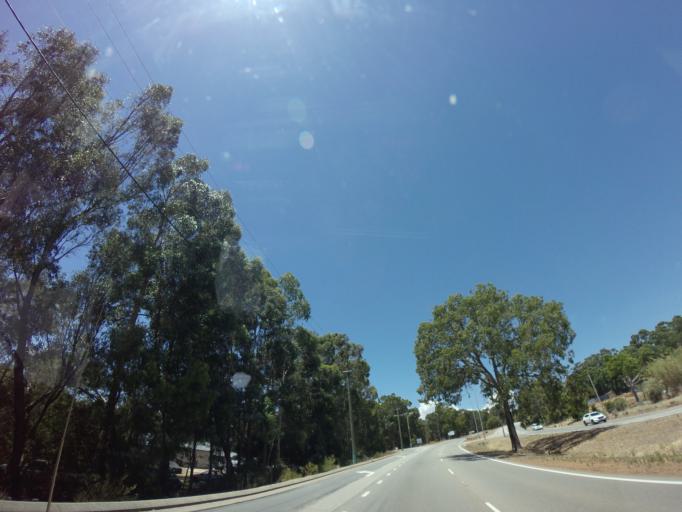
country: AU
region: Western Australia
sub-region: Mundaring
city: Parkerville
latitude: -31.8990
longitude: 116.1394
